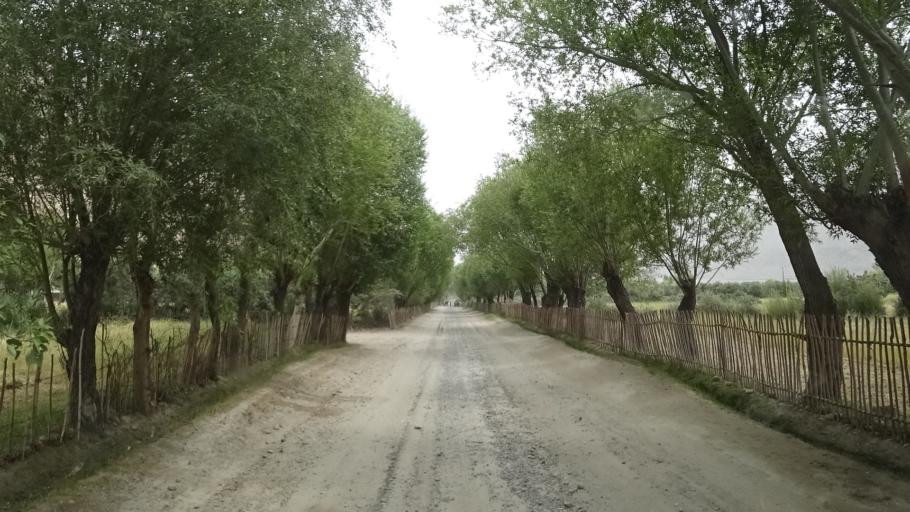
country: AF
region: Badakhshan
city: Khandud
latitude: 37.0219
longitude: 72.5880
